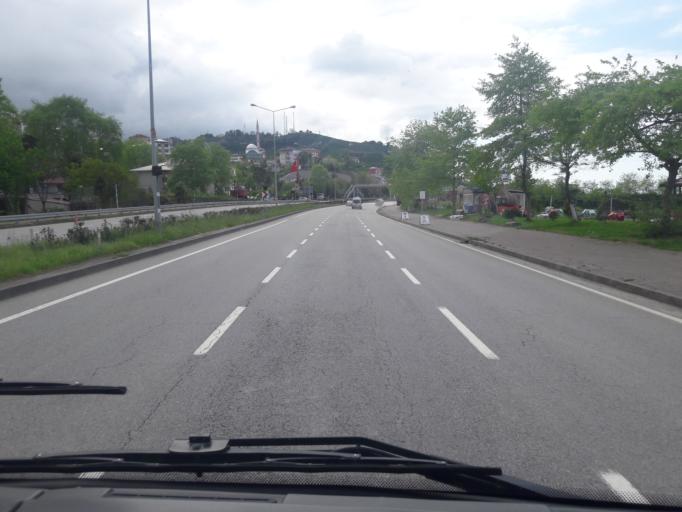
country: TR
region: Giresun
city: Piraziz
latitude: 40.9535
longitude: 38.1254
